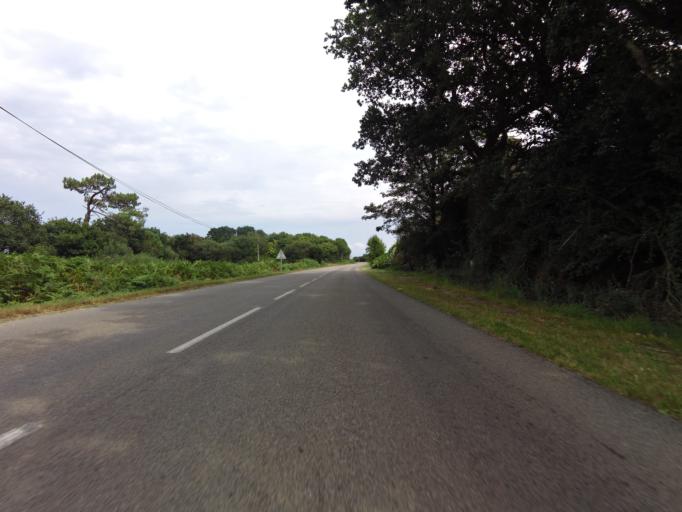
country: FR
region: Brittany
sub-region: Departement du Finistere
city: Poullan-sur-Mer
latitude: 48.0814
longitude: -4.4326
